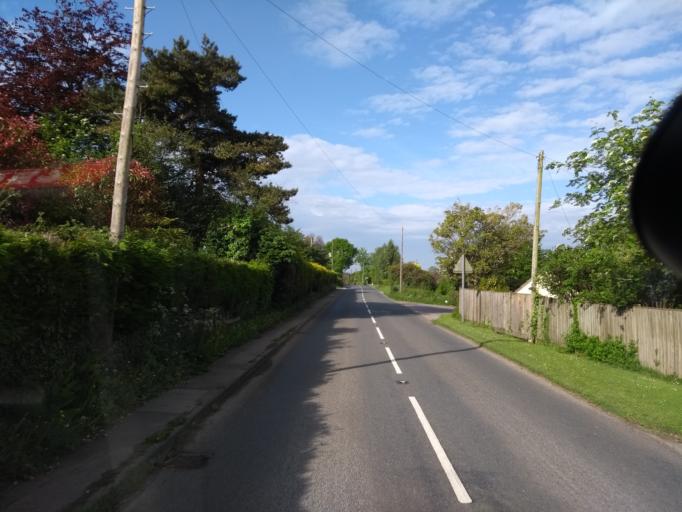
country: GB
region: England
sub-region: Devon
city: Axminster
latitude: 50.7672
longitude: -2.9556
